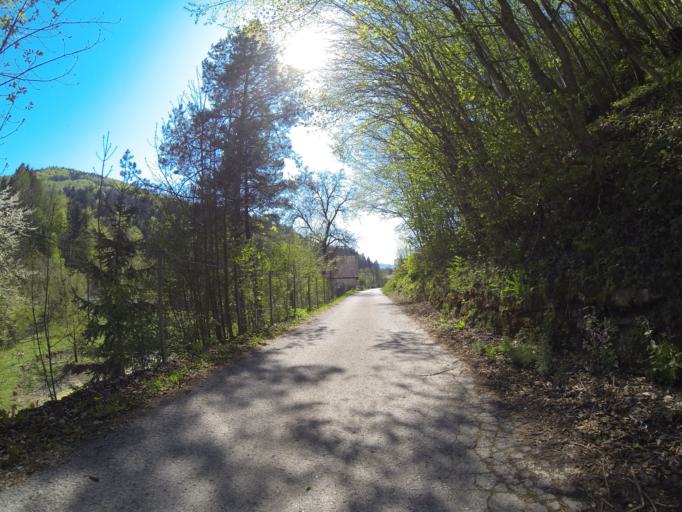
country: AT
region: Upper Austria
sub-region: Politischer Bezirk Gmunden
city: Altmunster
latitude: 47.9231
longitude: 13.7466
